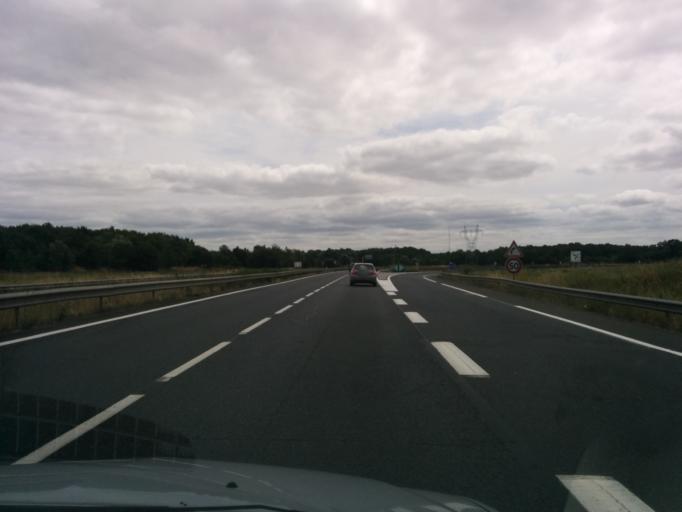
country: FR
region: Pays de la Loire
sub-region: Departement de la Loire-Atlantique
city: Basse-Goulaine
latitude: 47.2184
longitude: -1.4547
